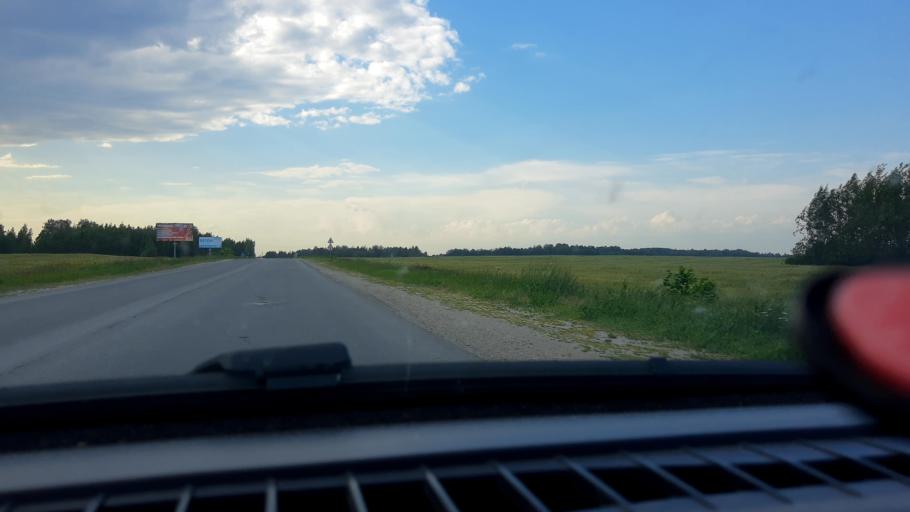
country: RU
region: Nizjnij Novgorod
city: Gorodets
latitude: 56.6567
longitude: 43.5029
